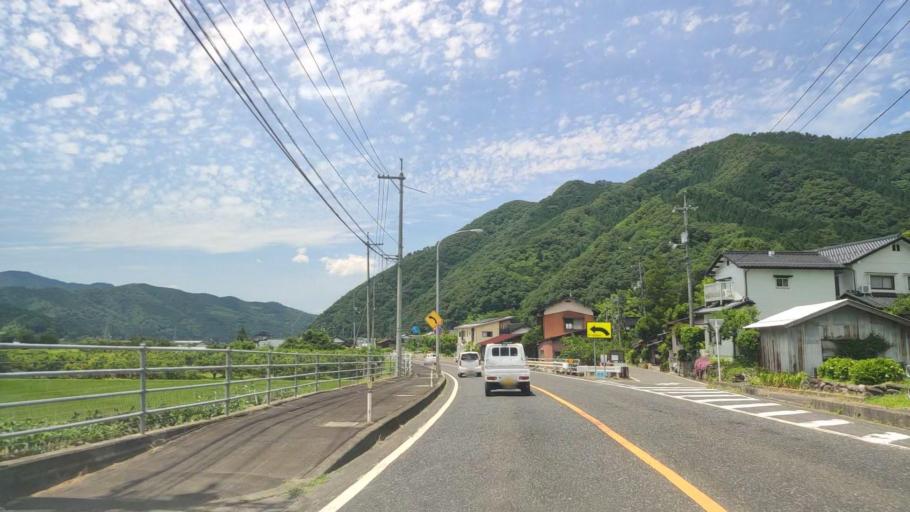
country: JP
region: Tottori
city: Tottori
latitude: 35.3663
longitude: 134.3390
